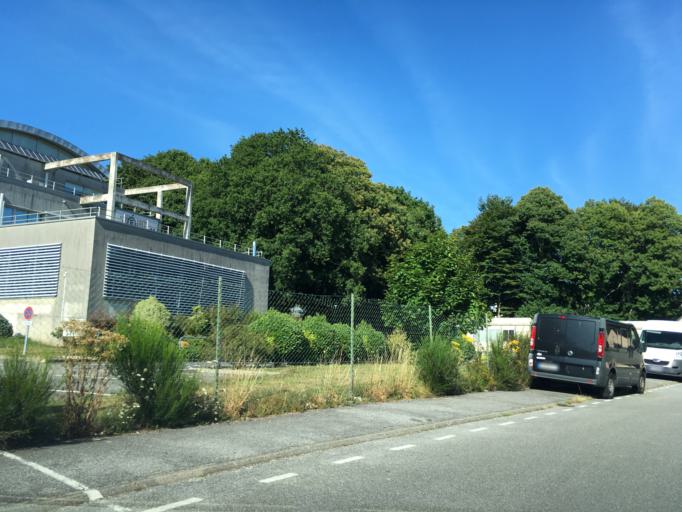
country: FR
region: Brittany
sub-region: Departement du Finistere
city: Quimper
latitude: 47.9863
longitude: -4.0876
